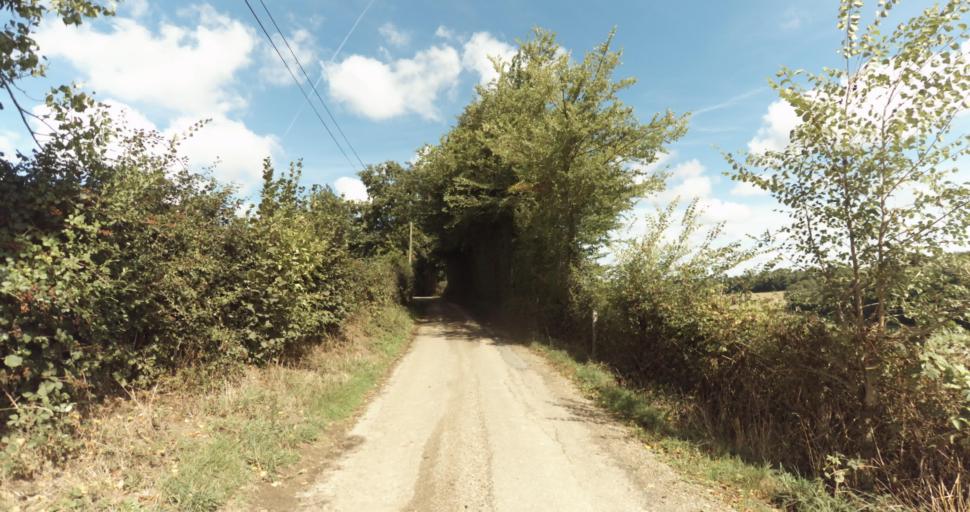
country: FR
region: Lower Normandy
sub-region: Departement du Calvados
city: Orbec
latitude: 48.9052
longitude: 0.3761
